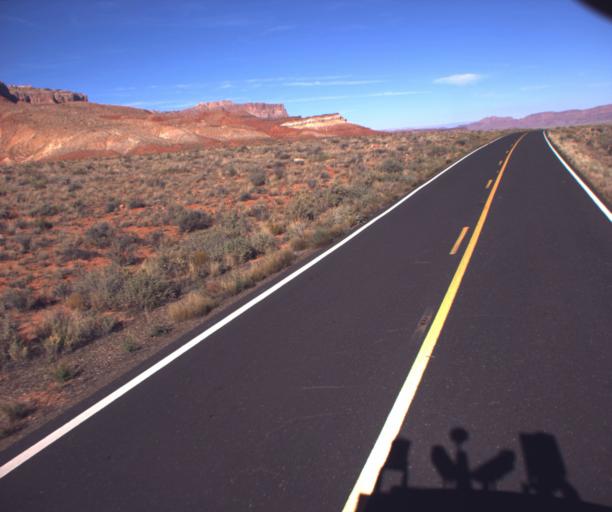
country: US
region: Arizona
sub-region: Coconino County
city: LeChee
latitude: 36.6954
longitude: -111.8103
